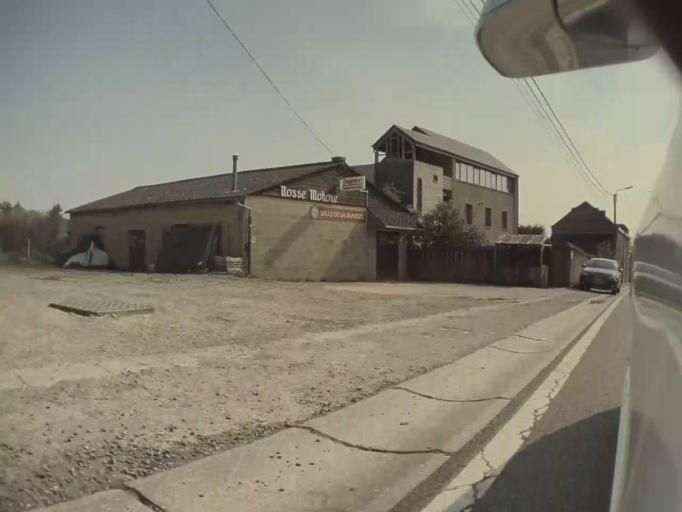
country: BE
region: Wallonia
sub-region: Province de Namur
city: Havelange
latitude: 50.3403
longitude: 5.2928
